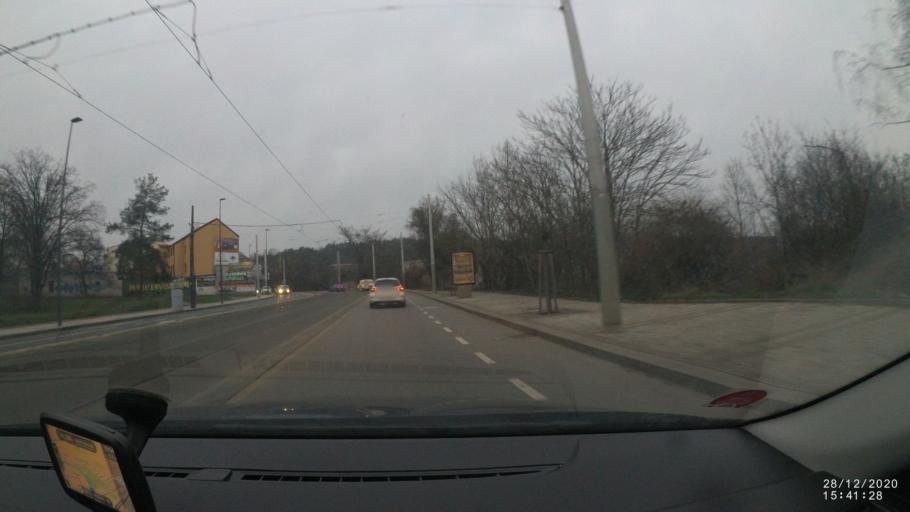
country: CZ
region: Praha
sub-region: Praha 8
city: Liben
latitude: 50.1127
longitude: 14.4762
